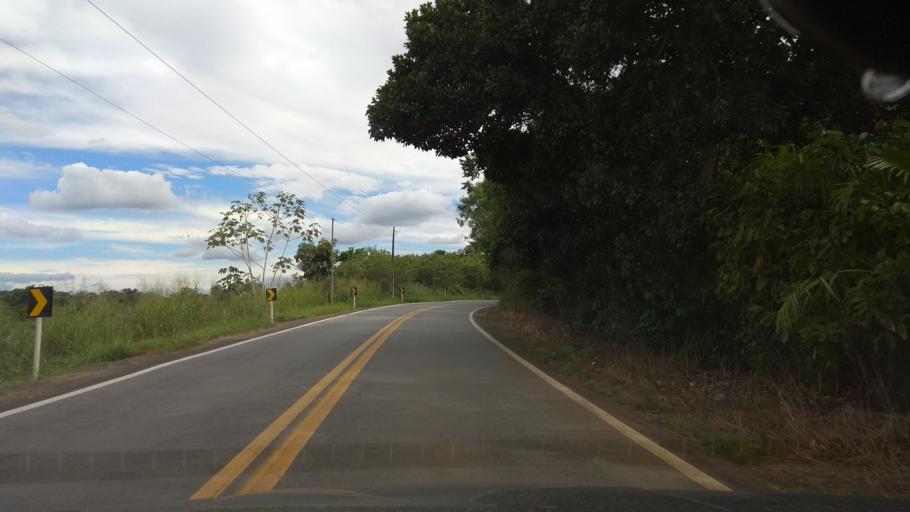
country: BR
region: Bahia
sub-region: Ubata
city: Ubata
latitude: -14.2014
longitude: -39.5700
